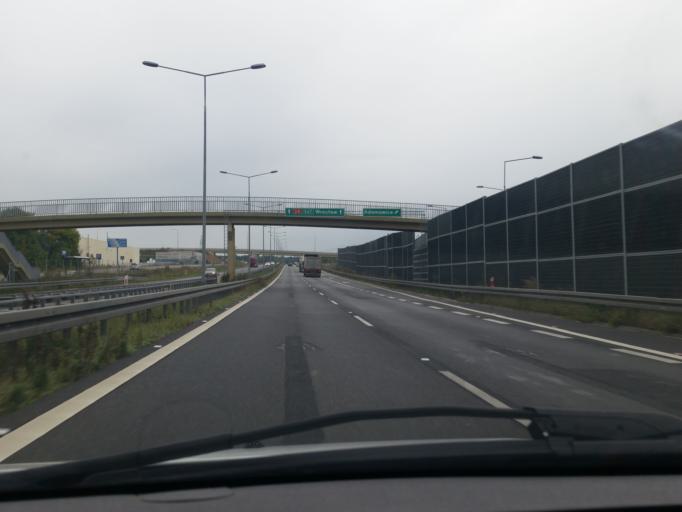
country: PL
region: Masovian Voivodeship
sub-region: Powiat zyrardowski
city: Mszczonow
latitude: 51.9412
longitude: 20.4816
